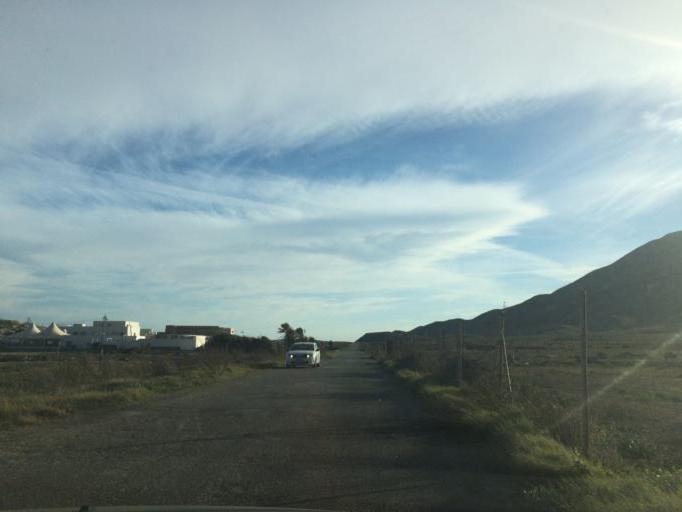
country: ES
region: Andalusia
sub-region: Provincia de Almeria
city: San Jose
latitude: 36.8057
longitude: -2.0646
